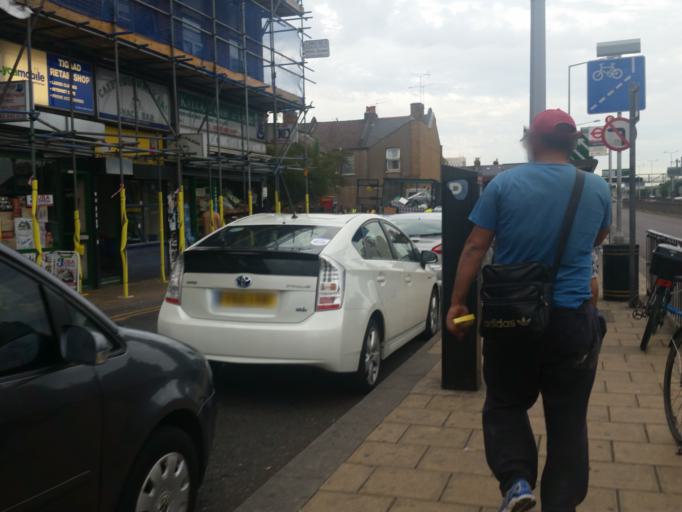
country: GB
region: England
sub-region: Greater London
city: Enfield
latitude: 51.6148
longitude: -0.0638
